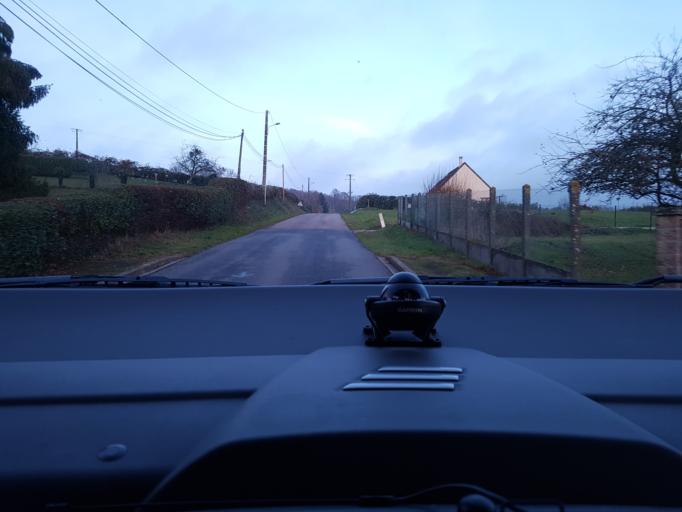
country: FR
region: Lower Normandy
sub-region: Departement de l'Orne
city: Tourouvre
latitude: 48.5999
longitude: 0.6613
